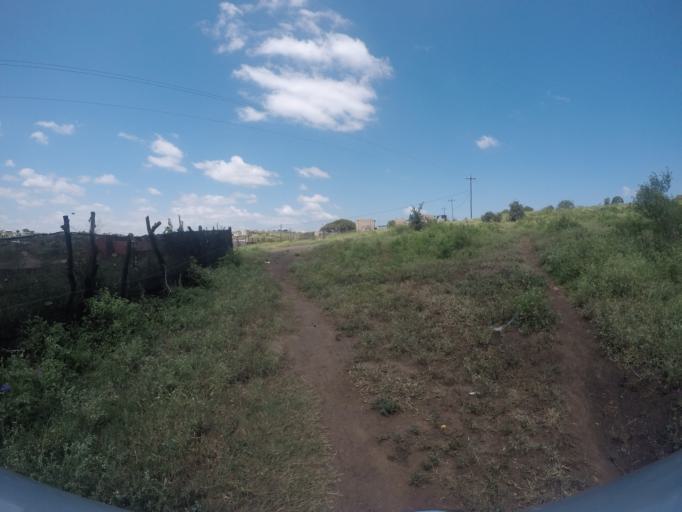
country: ZA
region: KwaZulu-Natal
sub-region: uThungulu District Municipality
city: Empangeni
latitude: -28.6032
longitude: 31.7361
